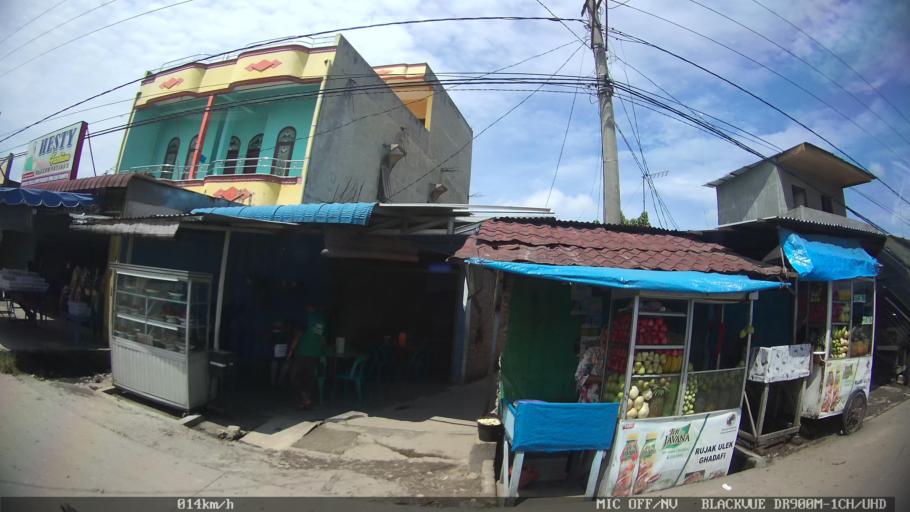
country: ID
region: North Sumatra
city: Medan
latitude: 3.5960
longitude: 98.7533
